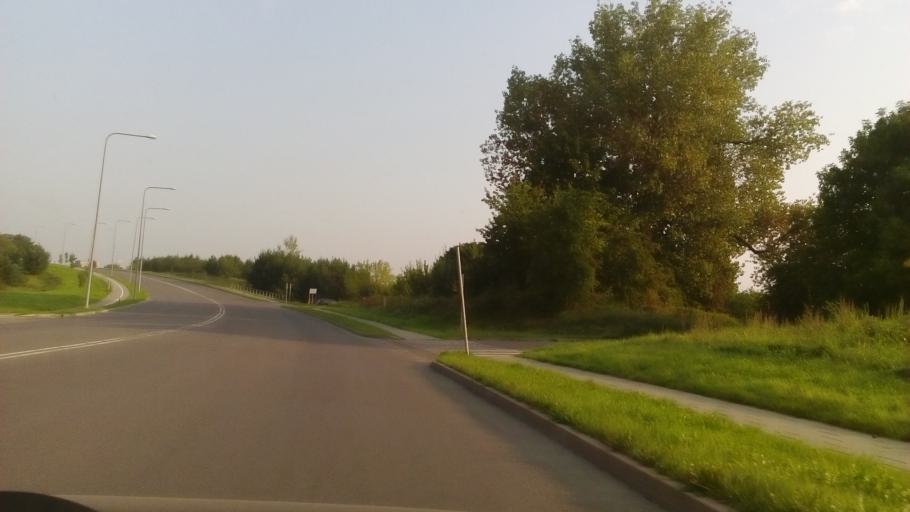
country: LT
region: Alytaus apskritis
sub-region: Alytus
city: Alytus
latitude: 54.4000
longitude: 24.0155
